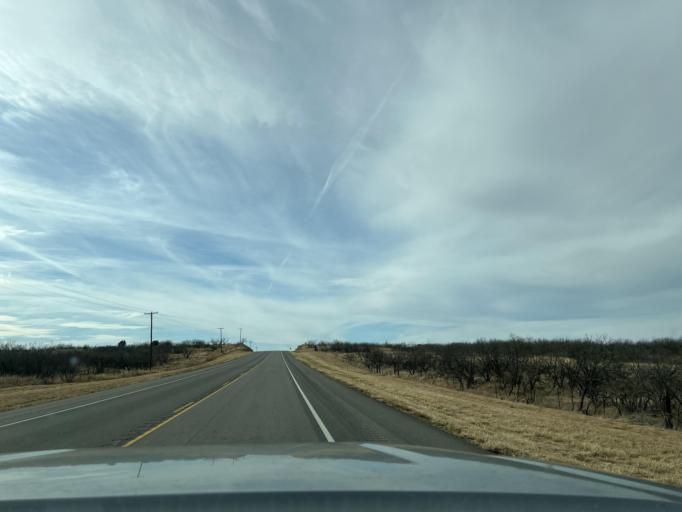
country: US
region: Texas
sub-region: Jones County
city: Anson
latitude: 32.7509
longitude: -99.7432
